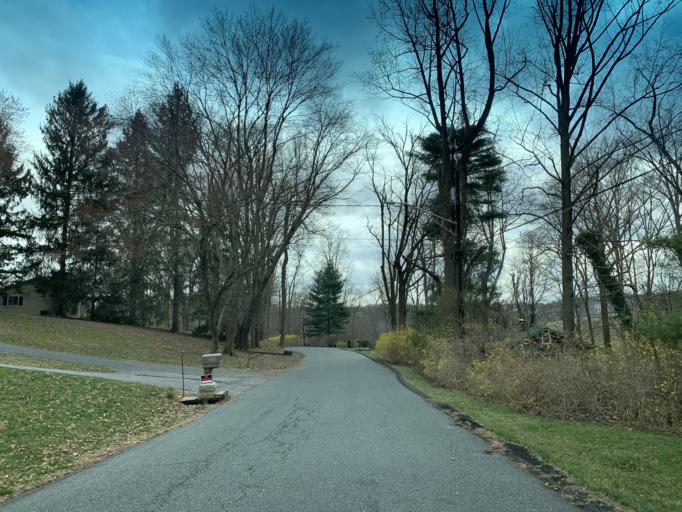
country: US
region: Maryland
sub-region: Harford County
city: North Bel Air
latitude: 39.5191
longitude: -76.3680
